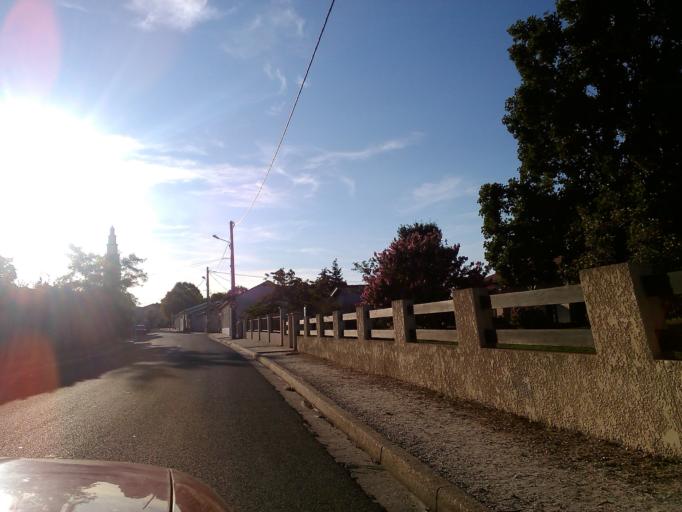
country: FR
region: Aquitaine
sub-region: Departement de la Gironde
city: Soulac-sur-Mer
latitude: 45.4303
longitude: -1.0330
